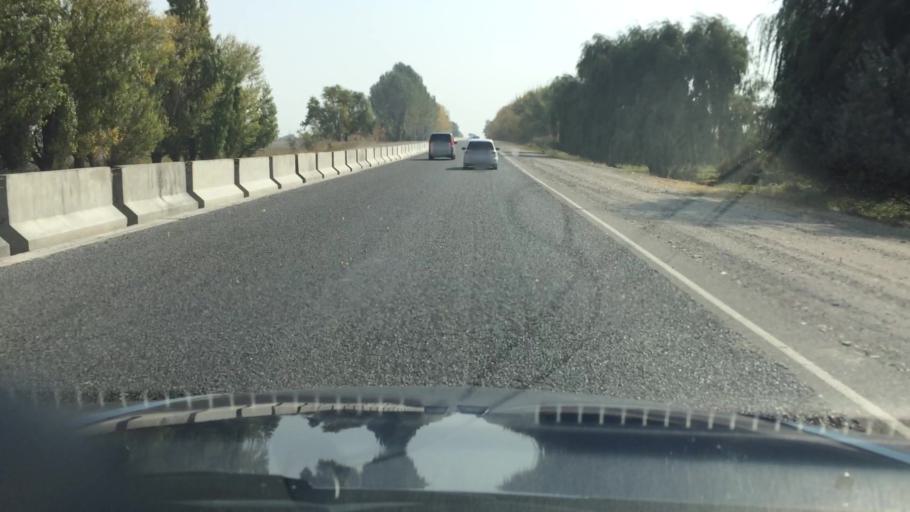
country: KG
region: Chuy
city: Kant
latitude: 42.9657
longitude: 74.9119
